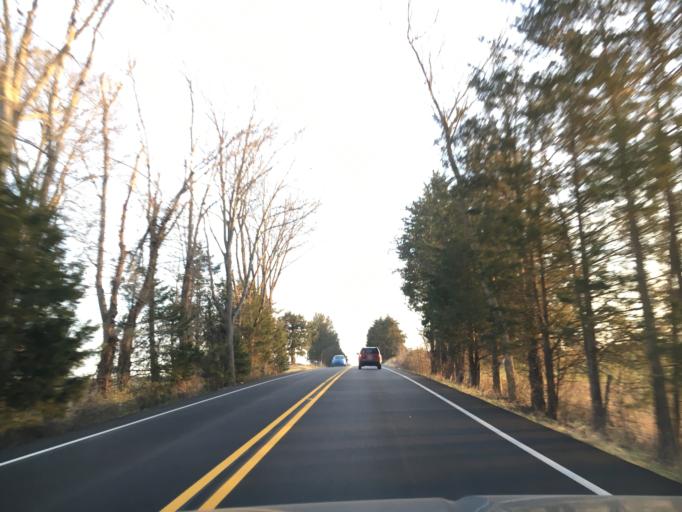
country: US
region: Virginia
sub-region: Orange County
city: Orange
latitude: 38.2041
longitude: -77.9438
